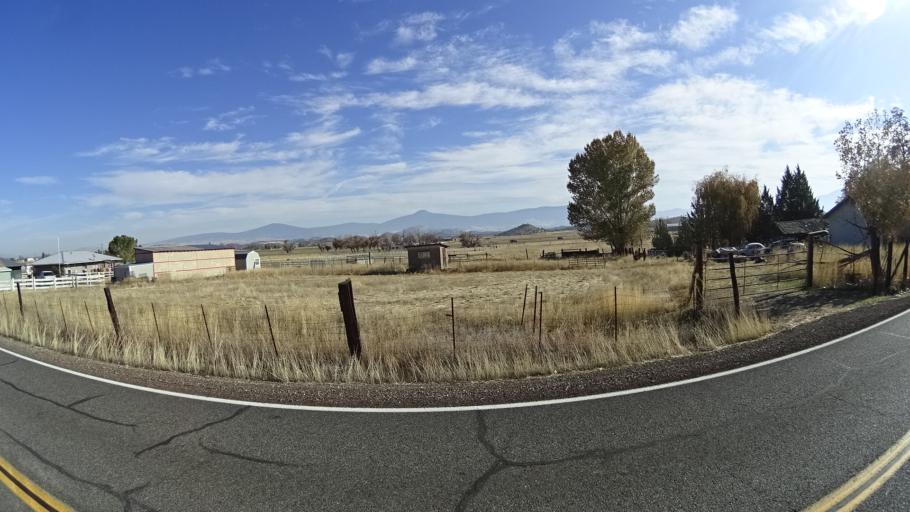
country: US
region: California
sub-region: Siskiyou County
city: Montague
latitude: 41.6333
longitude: -122.5303
